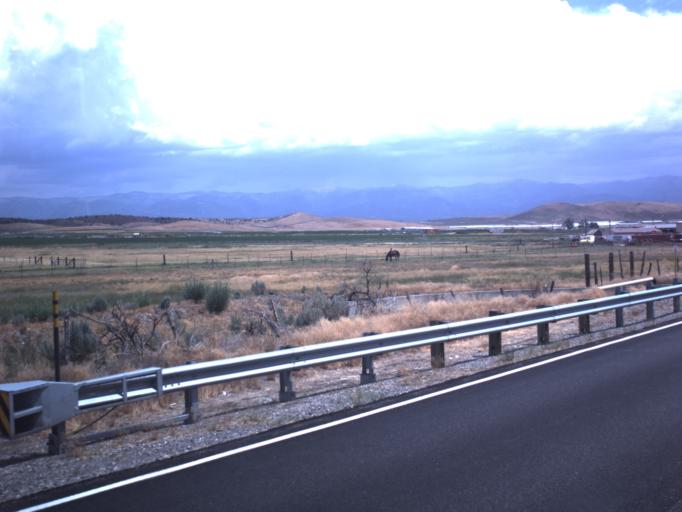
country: US
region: Utah
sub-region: Sanpete County
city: Moroni
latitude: 39.5767
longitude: -111.6101
